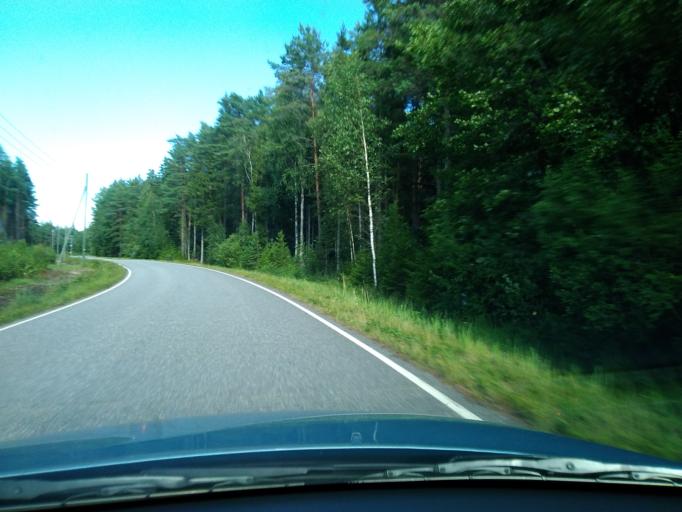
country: FI
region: Uusimaa
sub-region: Raaseporin
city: Hanko
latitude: 59.8379
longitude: 23.1598
